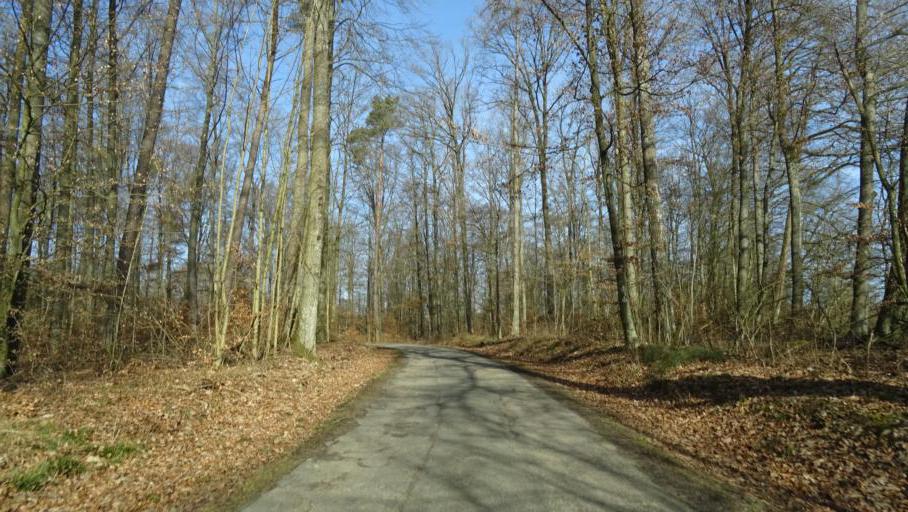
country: DE
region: Baden-Wuerttemberg
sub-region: Karlsruhe Region
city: Billigheim
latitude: 49.3627
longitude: 9.2504
